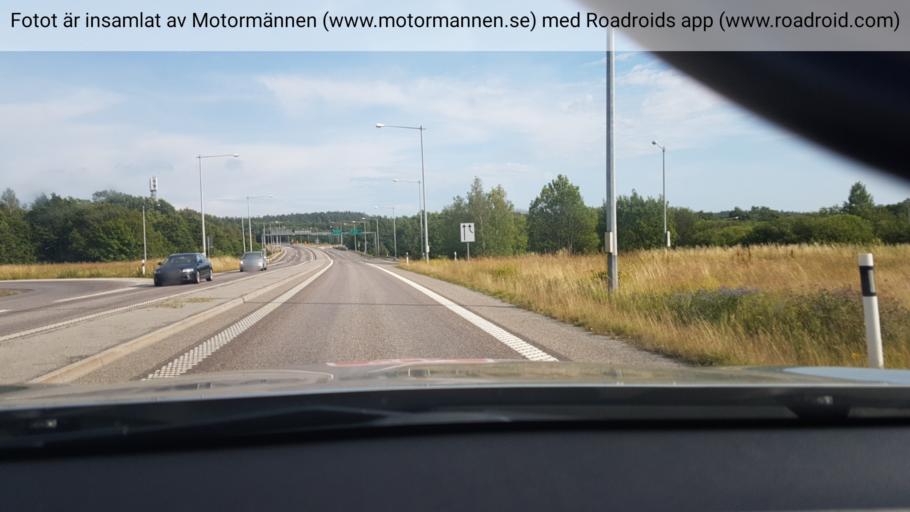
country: SE
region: Vaestra Goetaland
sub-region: Stenungsunds Kommun
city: Stenungsund
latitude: 58.0610
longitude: 11.8720
